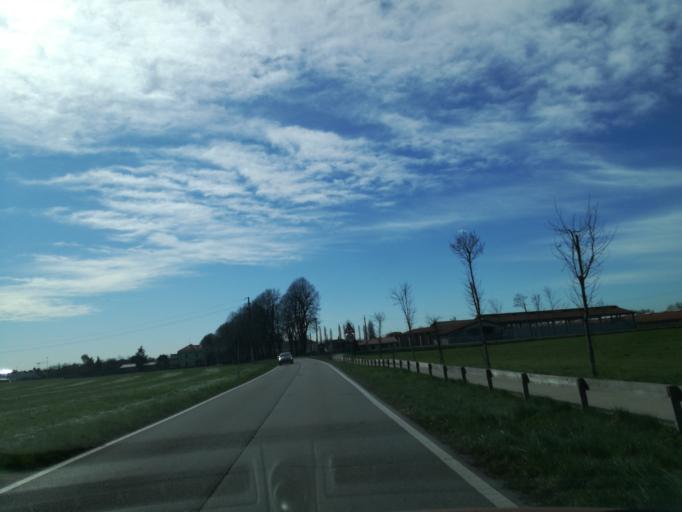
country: IT
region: Lombardy
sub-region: Provincia di Monza e Brianza
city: Villasanta
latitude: 45.6257
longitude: 9.3029
